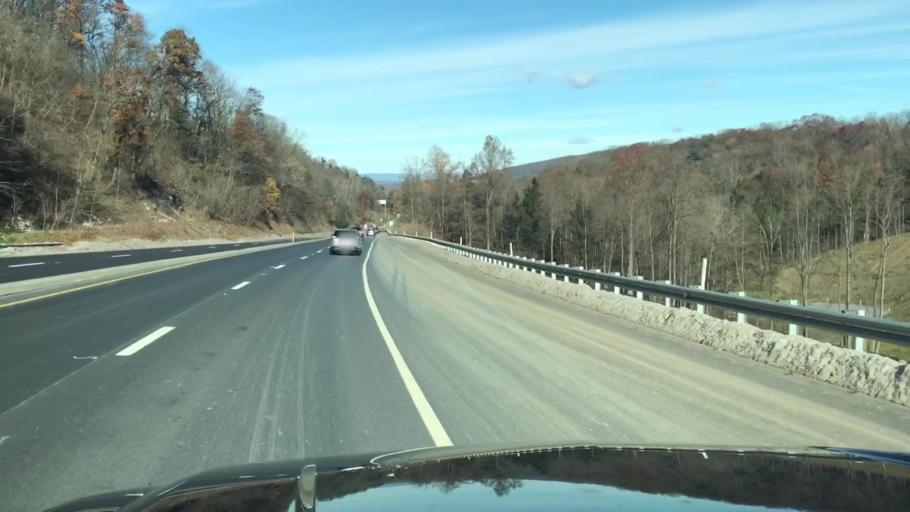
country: US
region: Pennsylvania
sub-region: Northumberland County
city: Northumberland
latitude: 40.8923
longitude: -76.8457
